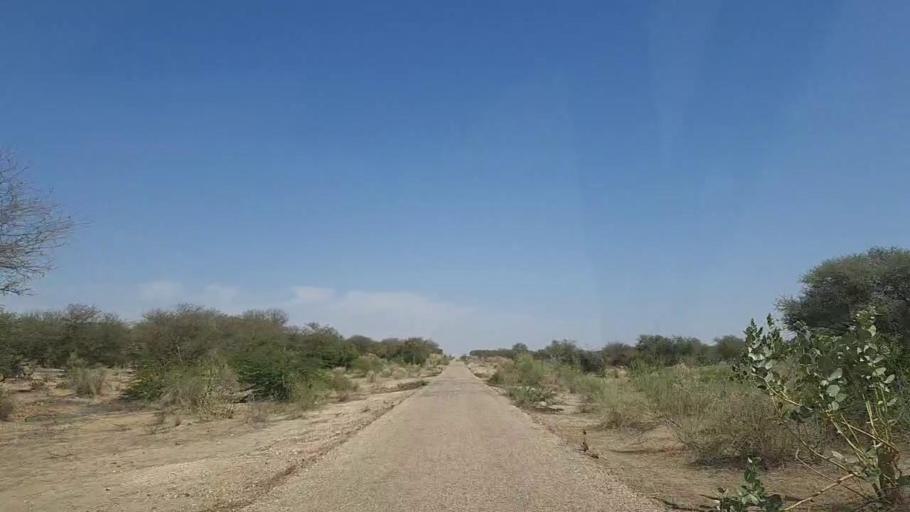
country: PK
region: Sindh
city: Mithi
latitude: 24.8293
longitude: 69.7089
